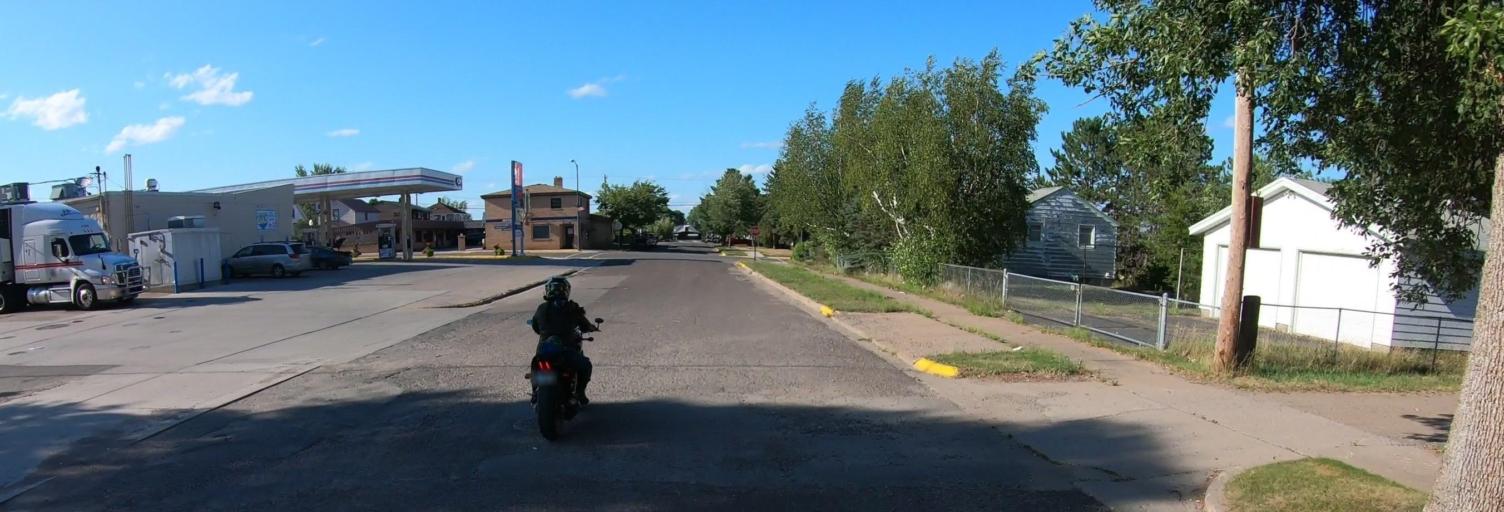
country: US
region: Minnesota
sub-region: Saint Louis County
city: Ely
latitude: 47.9024
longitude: -91.8505
